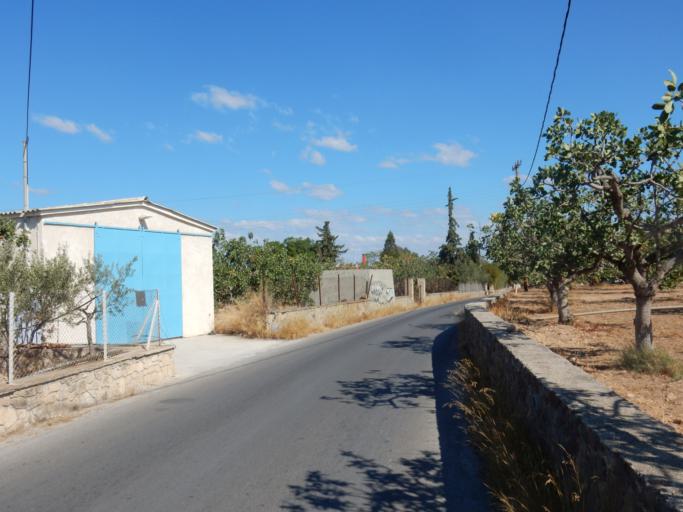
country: GR
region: Attica
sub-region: Nomos Piraios
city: Aegina
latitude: 37.7348
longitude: 23.4402
